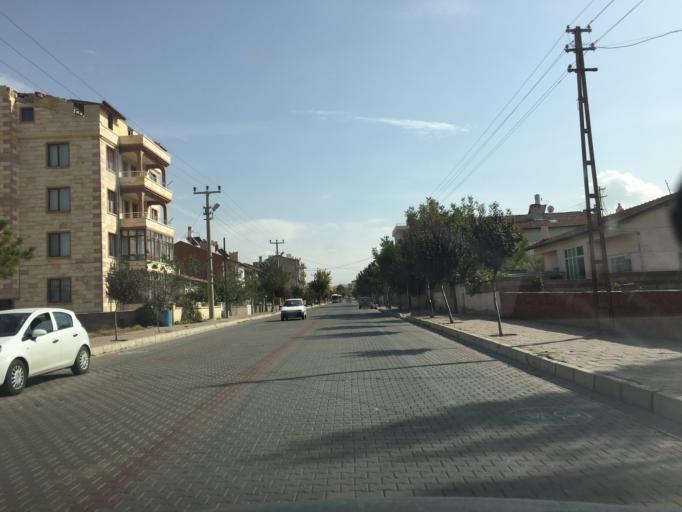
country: TR
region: Nevsehir
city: Avanos
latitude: 38.7116
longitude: 34.8462
